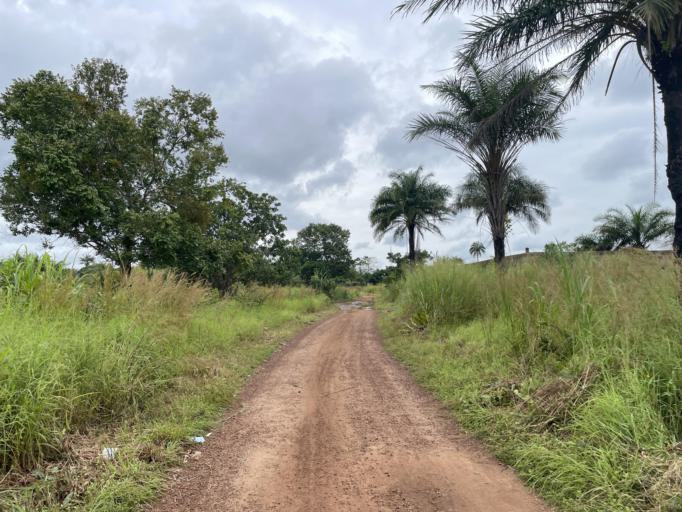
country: SL
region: Northern Province
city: Kambia
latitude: 9.1264
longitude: -12.8984
